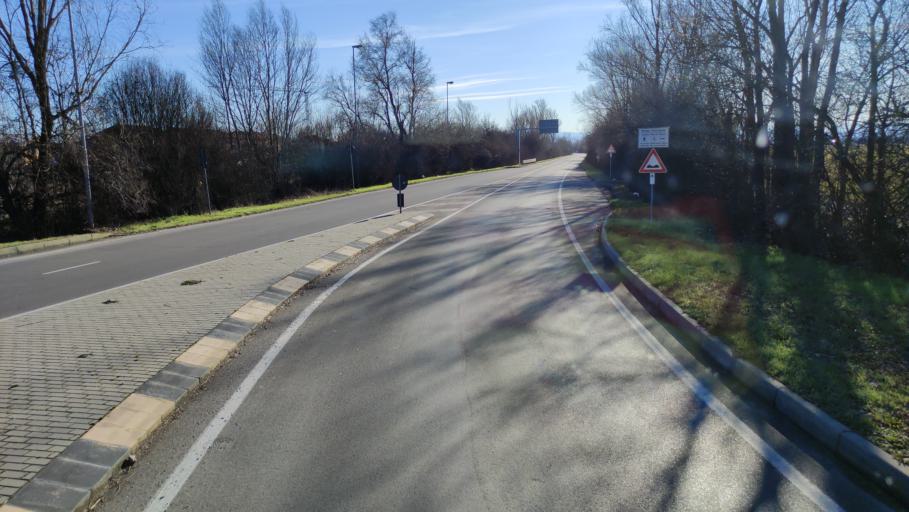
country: IT
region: Emilia-Romagna
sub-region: Provincia di Reggio Emilia
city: Bagnolo in Piano
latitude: 44.7674
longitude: 10.6645
